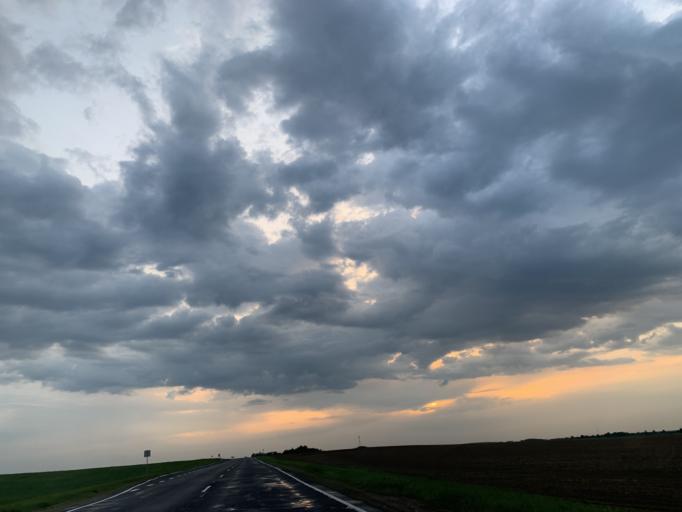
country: BY
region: Minsk
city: Nyasvizh
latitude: 53.1494
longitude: 26.8209
